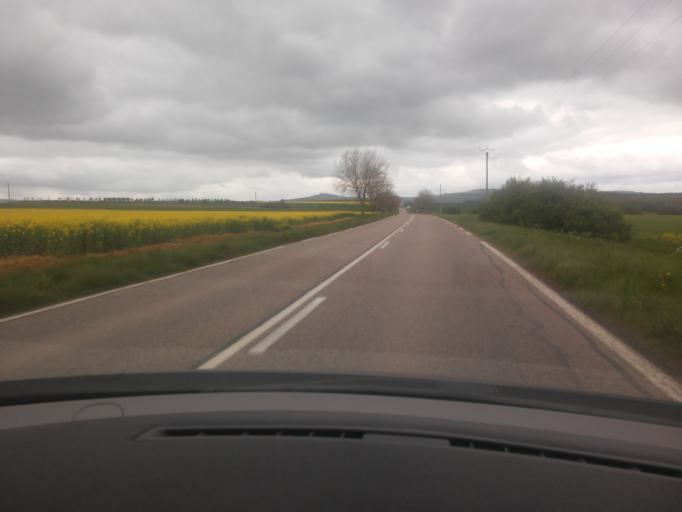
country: FR
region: Lorraine
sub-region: Departement de la Moselle
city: Verny
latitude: 48.9562
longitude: 6.1782
